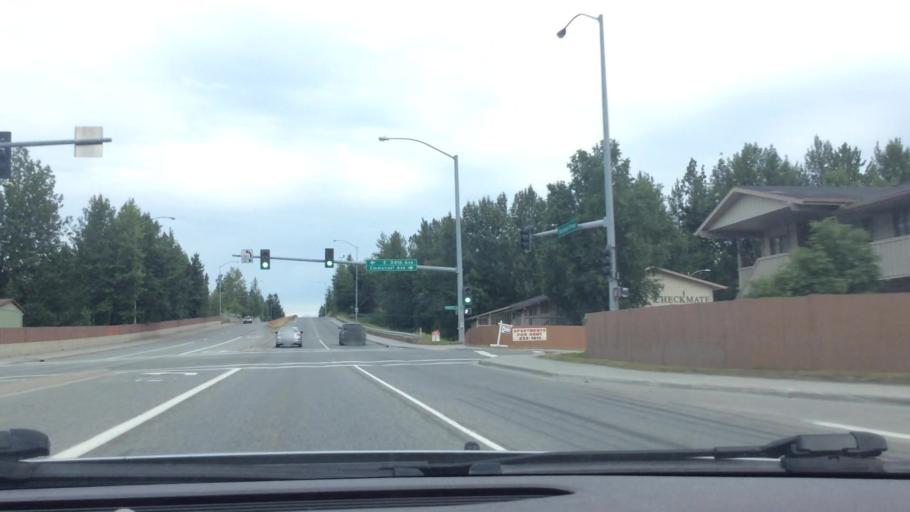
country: US
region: Alaska
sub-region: Anchorage Municipality
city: Anchorage
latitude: 61.1902
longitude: -149.7784
